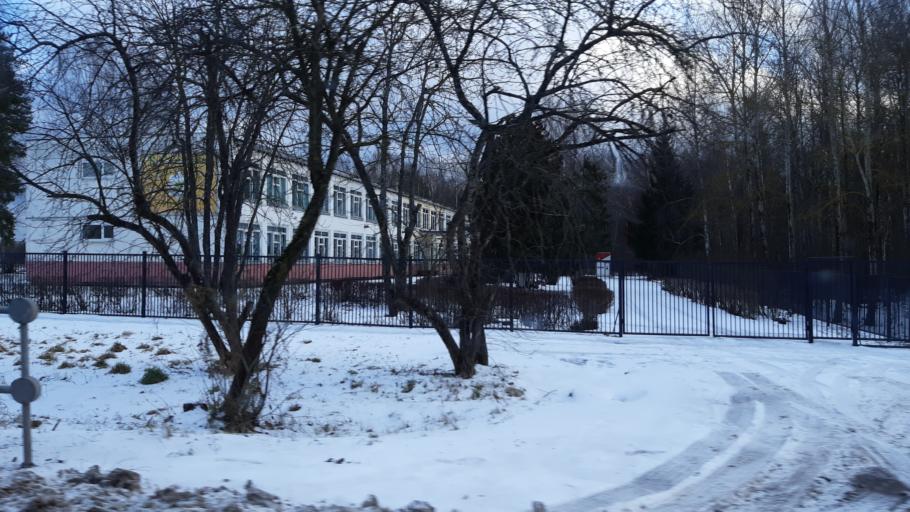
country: RU
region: Moskovskaya
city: Noginsk-9
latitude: 55.9996
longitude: 38.5472
